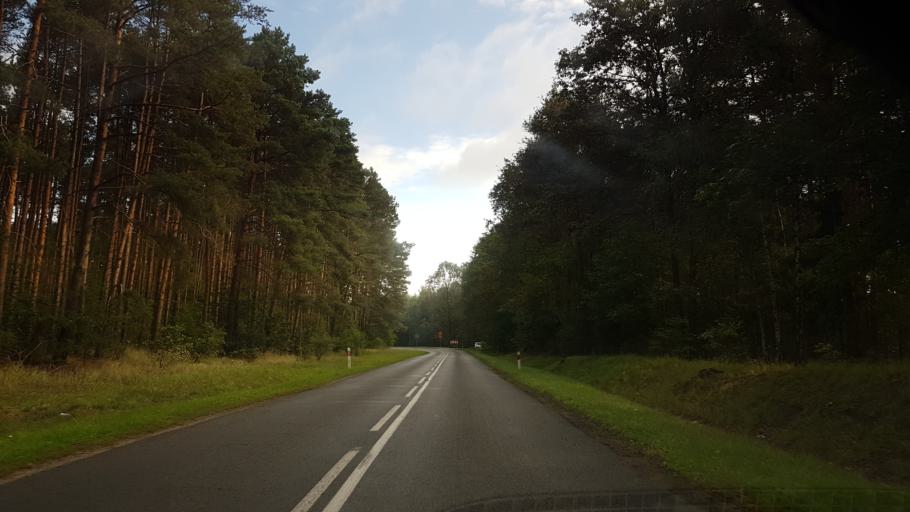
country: PL
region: Greater Poland Voivodeship
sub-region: Leszno
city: Leszno
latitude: 51.8009
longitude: 16.5796
